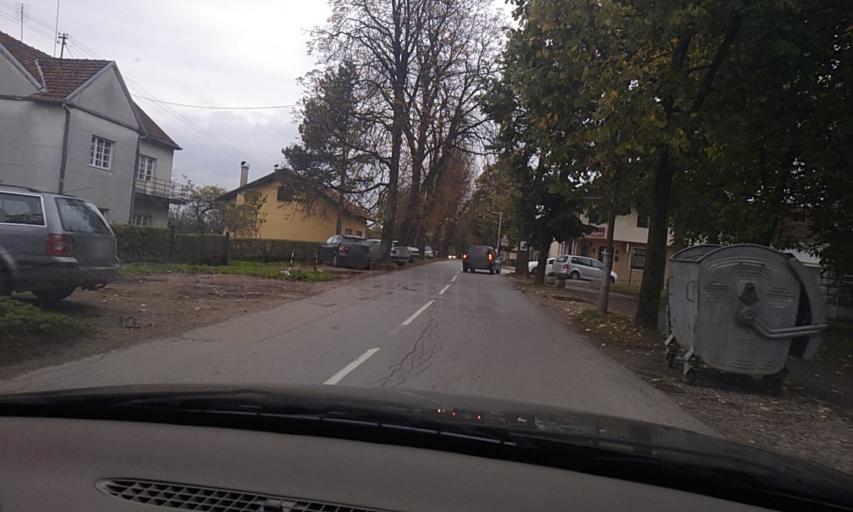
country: BA
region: Republika Srpska
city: Prnjavor
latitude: 44.8708
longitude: 17.6668
